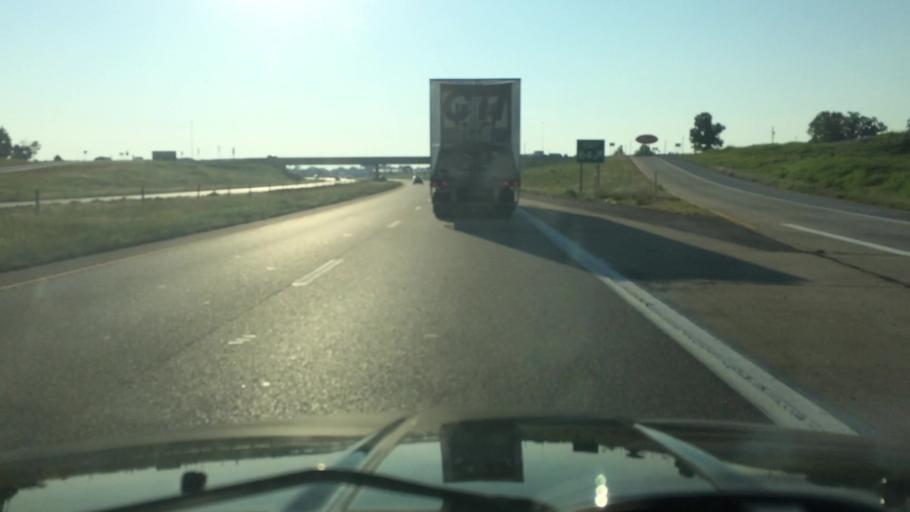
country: US
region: Missouri
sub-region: Greene County
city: Strafford
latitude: 37.2502
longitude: -93.1864
